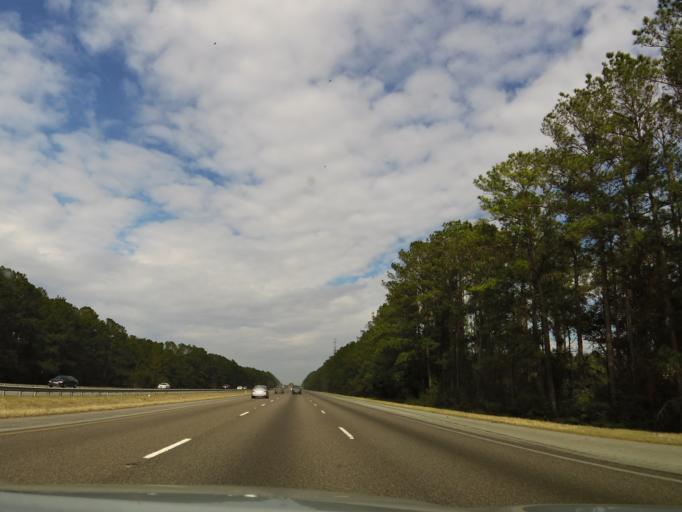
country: US
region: Georgia
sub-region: Liberty County
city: Midway
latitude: 31.8464
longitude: -81.3458
